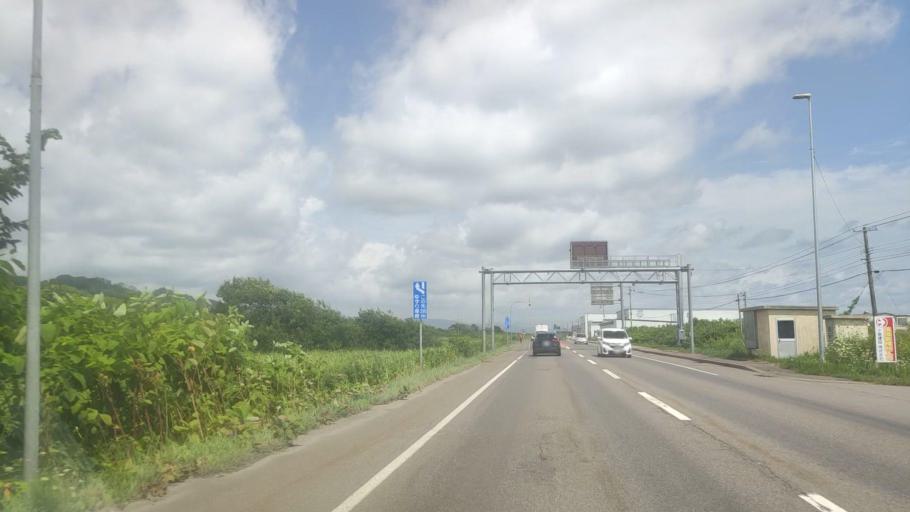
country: JP
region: Hokkaido
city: Niseko Town
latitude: 42.4426
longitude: 140.3264
